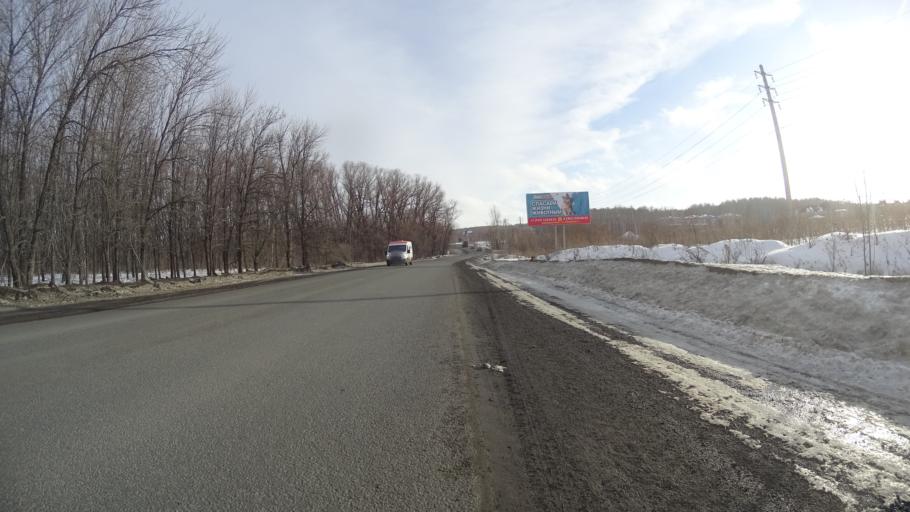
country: RU
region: Chelyabinsk
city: Sargazy
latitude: 55.1386
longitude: 61.2825
